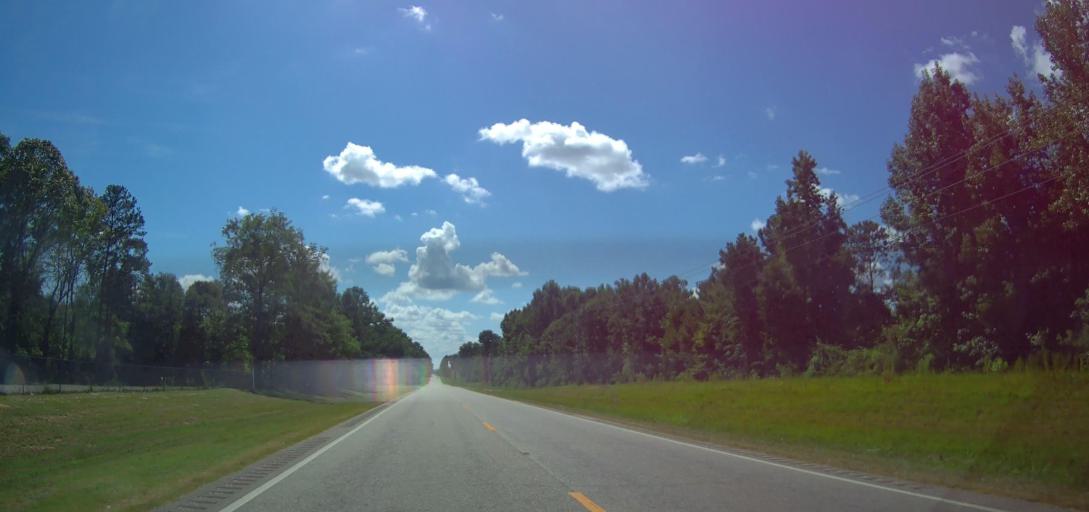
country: US
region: Alabama
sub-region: Elmore County
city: Tallassee
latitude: 32.3987
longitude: -85.9246
